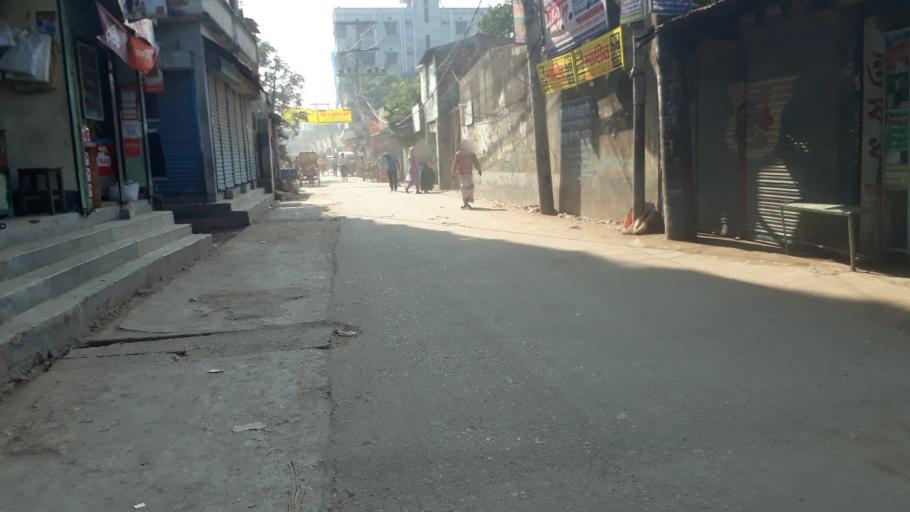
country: BD
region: Dhaka
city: Tungi
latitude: 23.8487
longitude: 90.2518
